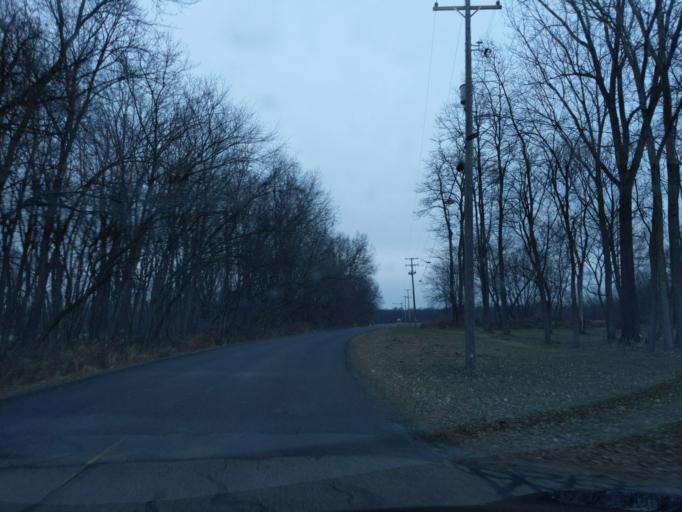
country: US
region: Michigan
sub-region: Ionia County
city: Portland
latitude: 42.9861
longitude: -84.9444
